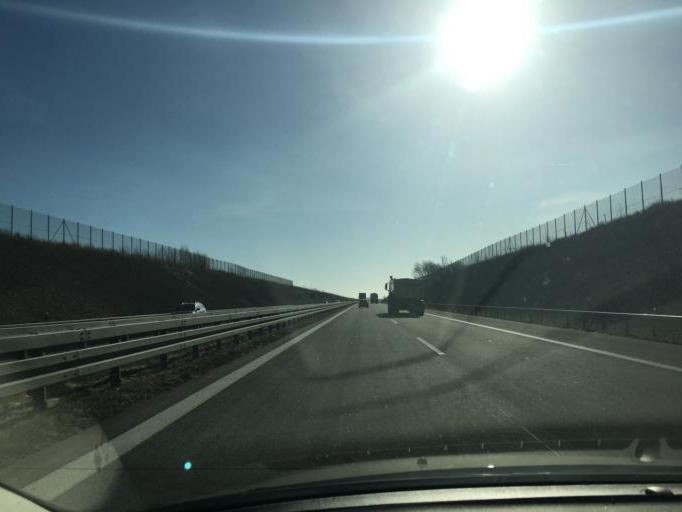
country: DE
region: Saxony
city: Geithain
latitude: 51.0462
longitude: 12.6578
